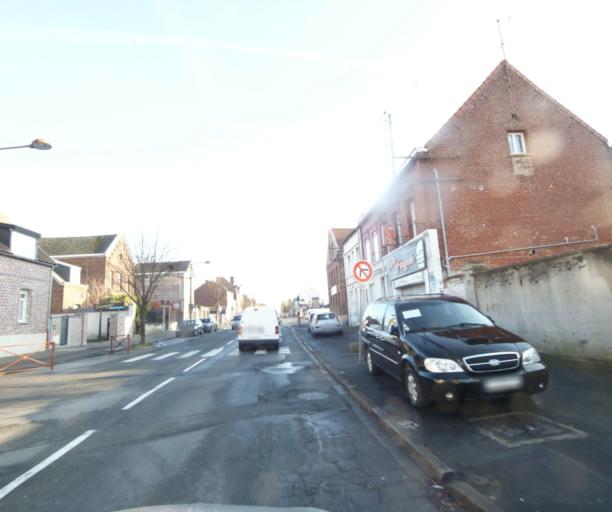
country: FR
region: Nord-Pas-de-Calais
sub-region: Departement du Nord
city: Marly
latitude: 50.3507
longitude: 3.5429
